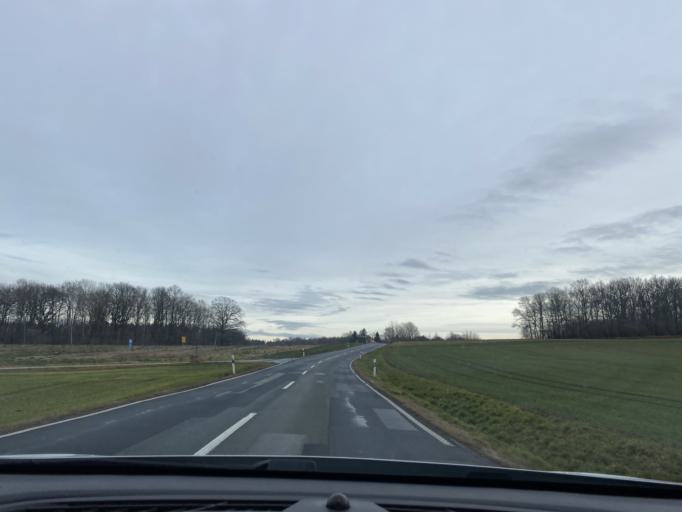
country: DE
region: Saxony
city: Reichenbach
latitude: 51.1288
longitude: 14.8087
